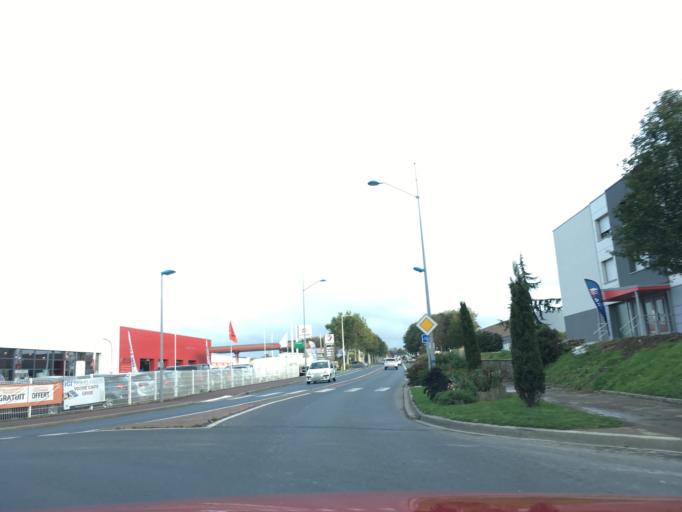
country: FR
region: Lower Normandy
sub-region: Departement de la Manche
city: Donville-les-Bains
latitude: 48.8378
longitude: -1.5665
